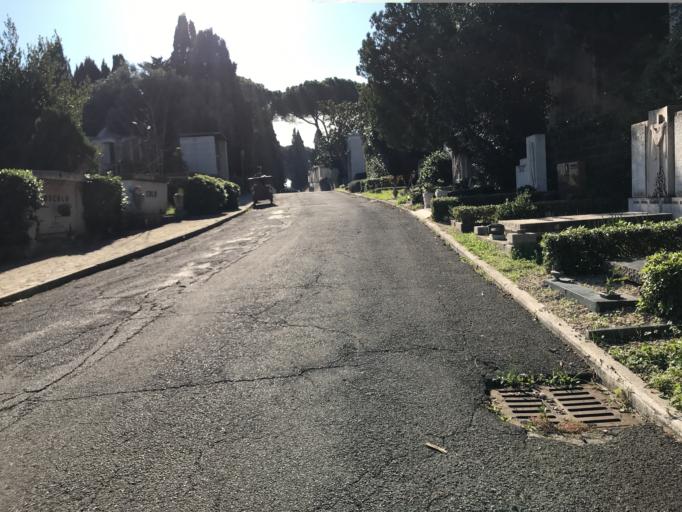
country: IT
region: Latium
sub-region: Citta metropolitana di Roma Capitale
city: Rome
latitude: 41.9005
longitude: 12.5234
